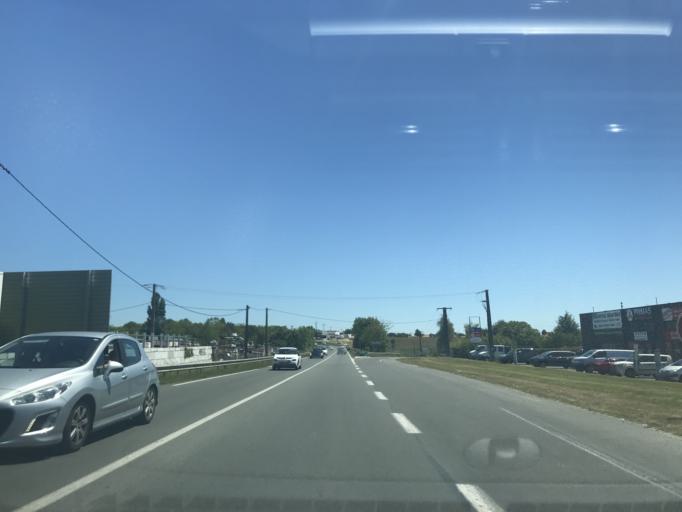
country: FR
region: Poitou-Charentes
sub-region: Departement de la Charente-Maritime
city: Vaux-sur-Mer
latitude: 45.6474
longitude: -1.0461
